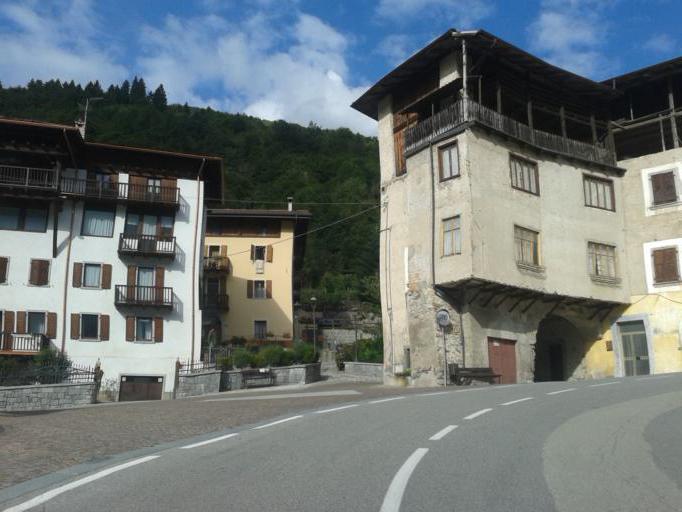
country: IT
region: Trentino-Alto Adige
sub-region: Provincia di Trento
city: Cimego
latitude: 45.9105
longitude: 10.6121
